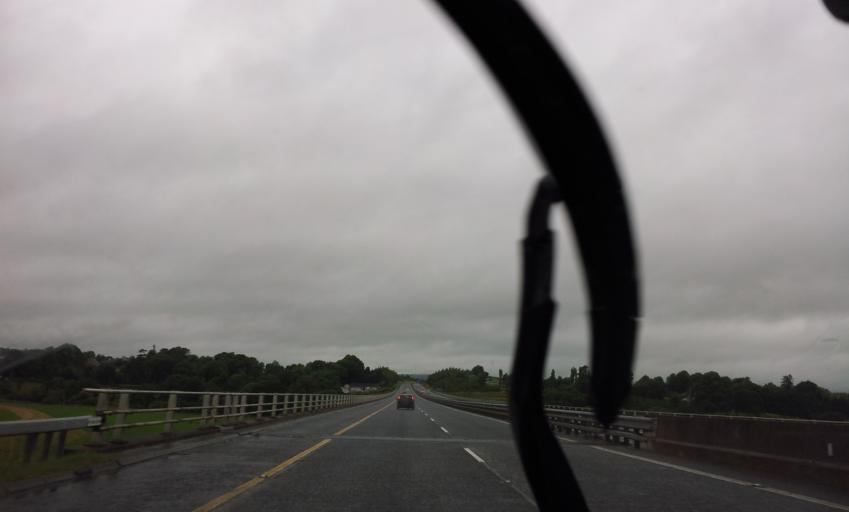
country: IE
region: Munster
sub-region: County Cork
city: Fermoy
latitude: 52.1374
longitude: -8.2612
